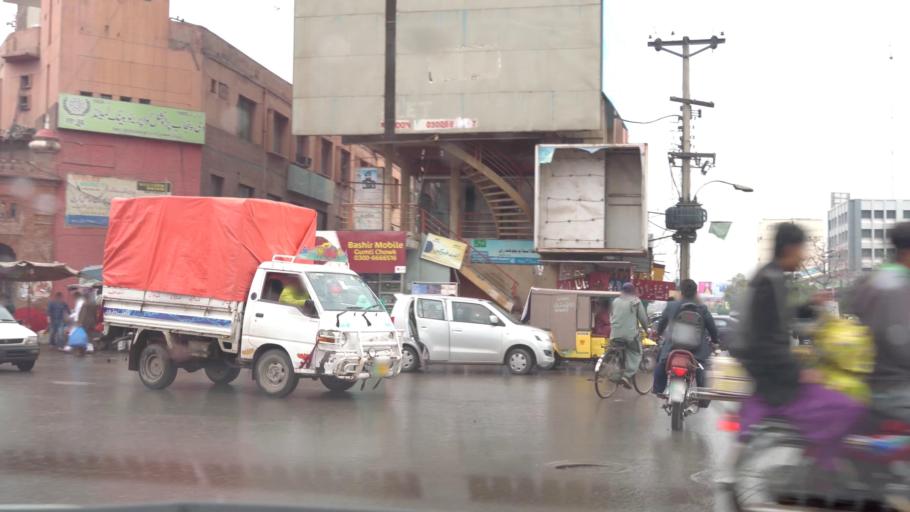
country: PK
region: Punjab
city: Faisalabad
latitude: 31.4167
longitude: 73.0886
